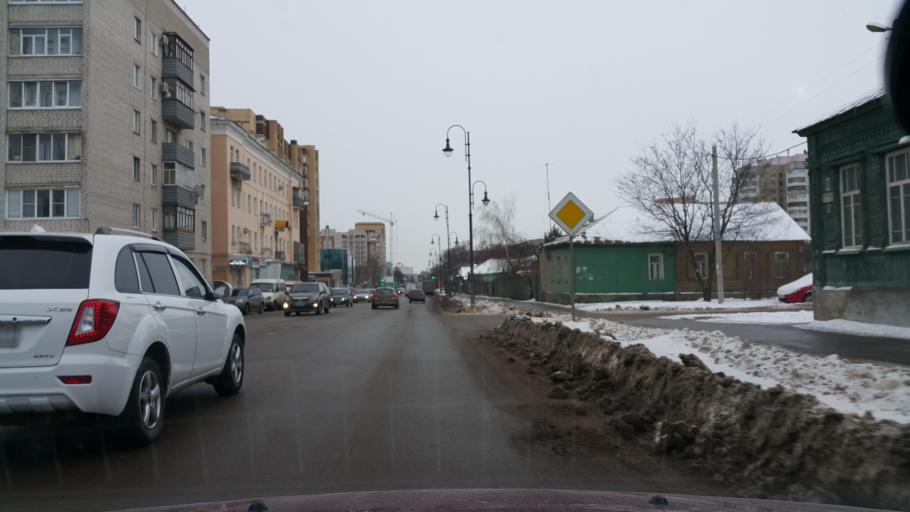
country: RU
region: Tambov
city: Tambov
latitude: 52.7356
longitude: 41.4482
